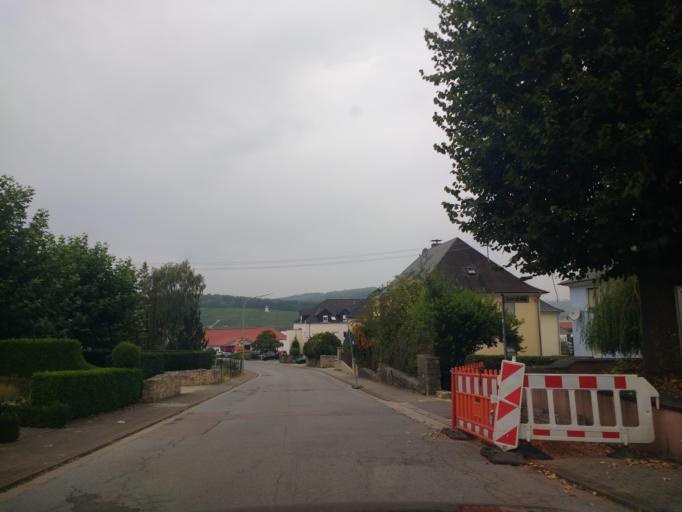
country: DE
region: Saarland
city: Perl
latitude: 49.4734
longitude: 6.3769
